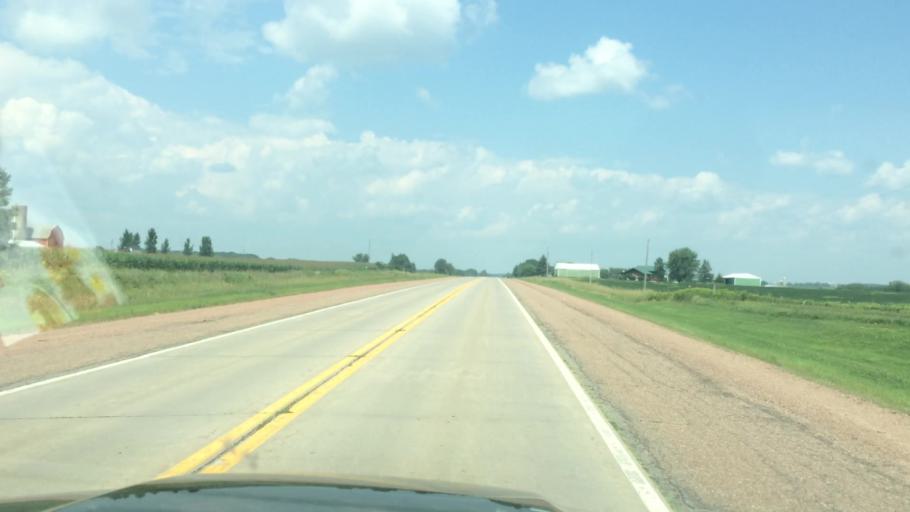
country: US
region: Wisconsin
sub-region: Clark County
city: Colby
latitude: 44.8621
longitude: -90.3158
